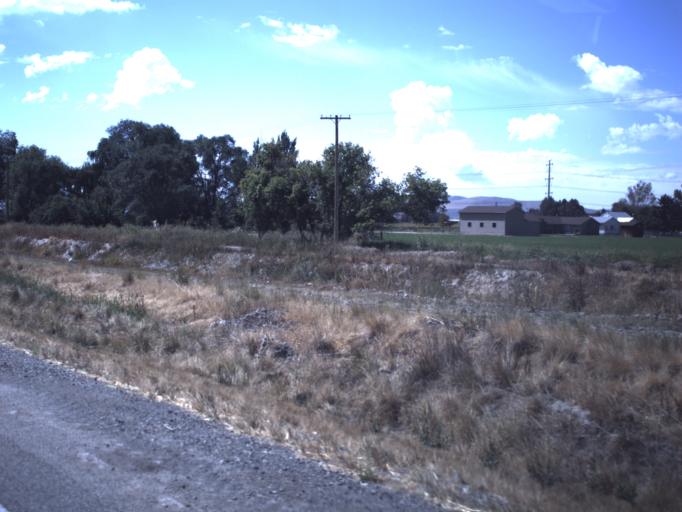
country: US
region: Utah
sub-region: Box Elder County
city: Elwood
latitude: 41.6851
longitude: -112.1414
